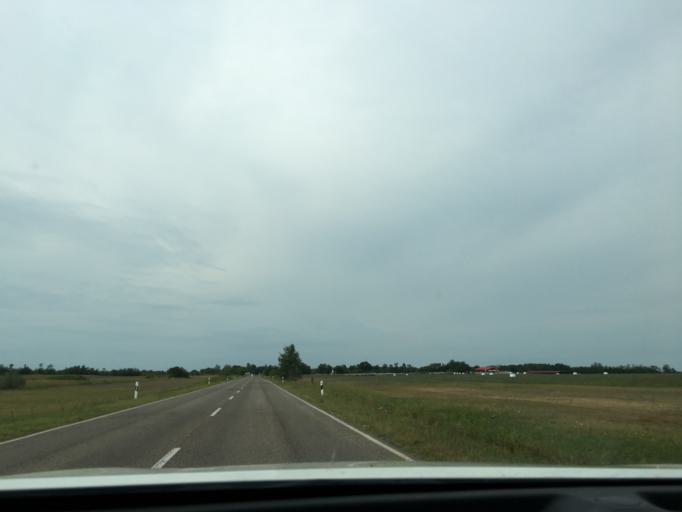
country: HU
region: Hajdu-Bihar
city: Egyek
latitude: 47.5825
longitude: 20.8539
